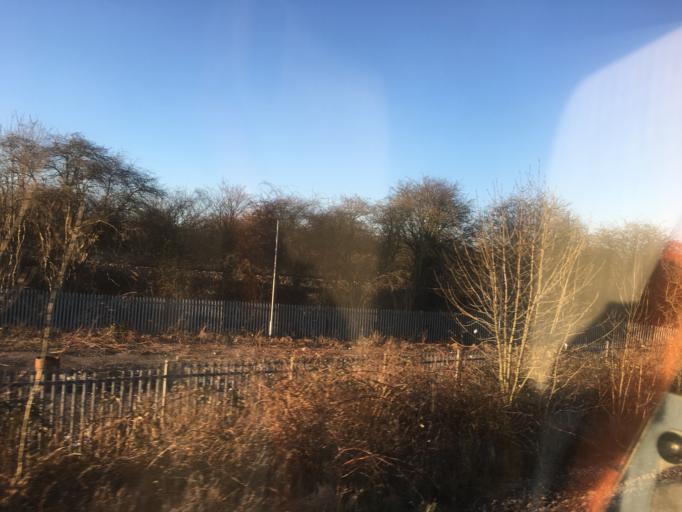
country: GB
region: England
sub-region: Derbyshire
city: Long Eaton
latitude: 52.8934
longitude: -1.2528
